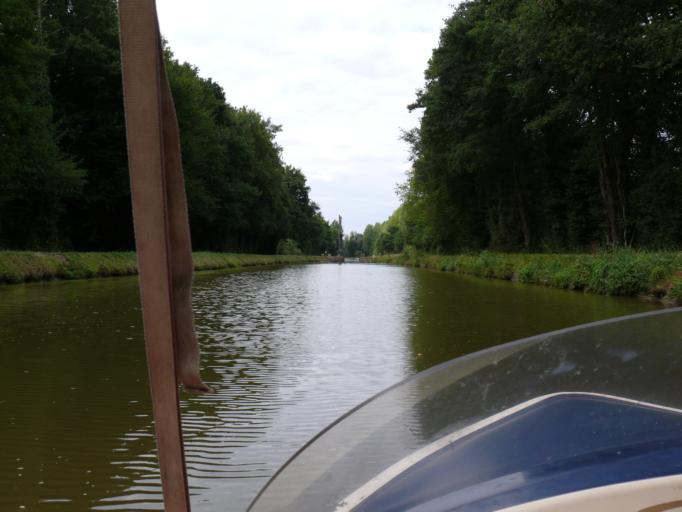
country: FR
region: Auvergne
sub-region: Departement de l'Allier
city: Vallon-en-Sully
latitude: 46.5175
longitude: 2.6142
